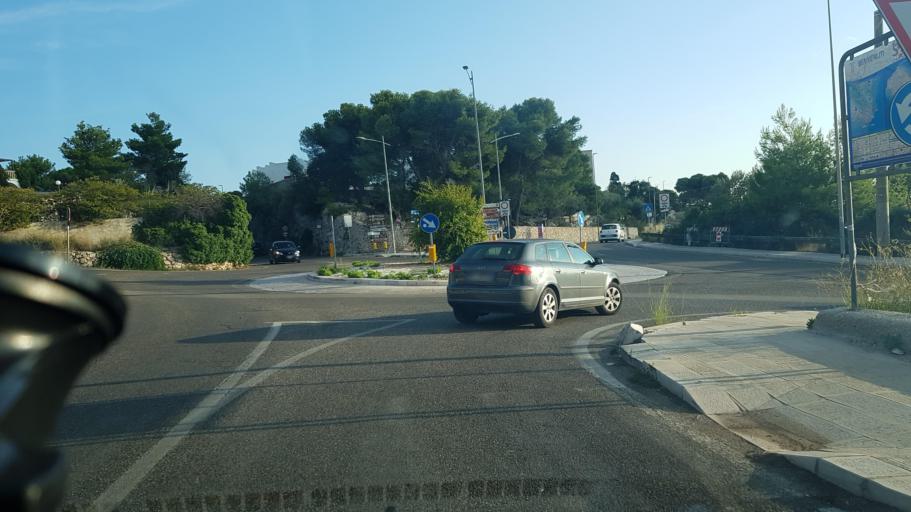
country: IT
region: Apulia
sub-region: Provincia di Lecce
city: Leuca
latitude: 39.7990
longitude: 18.3682
